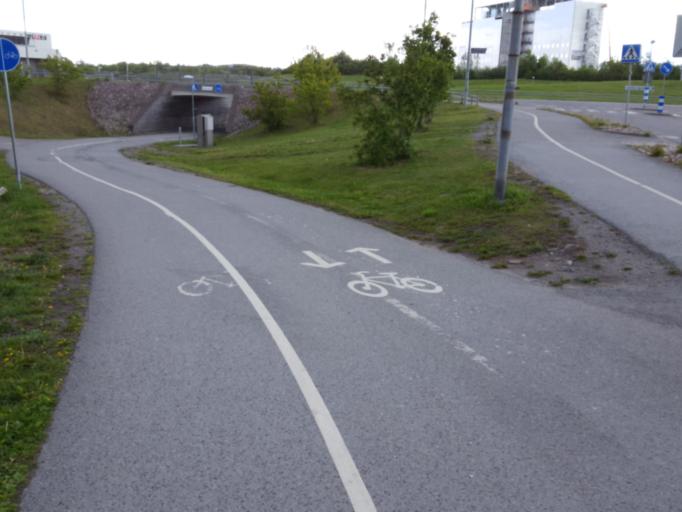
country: SE
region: Uppsala
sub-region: Uppsala Kommun
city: Gamla Uppsala
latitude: 59.8860
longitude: 17.6567
